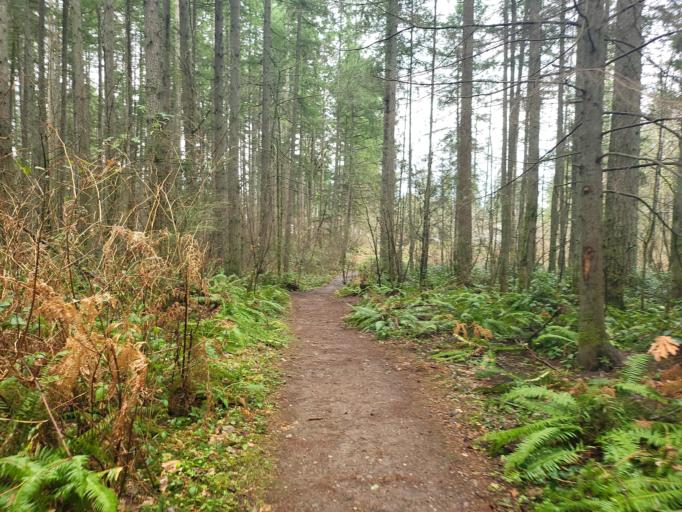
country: US
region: Washington
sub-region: King County
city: East Renton Highlands
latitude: 47.4803
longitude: -122.1454
